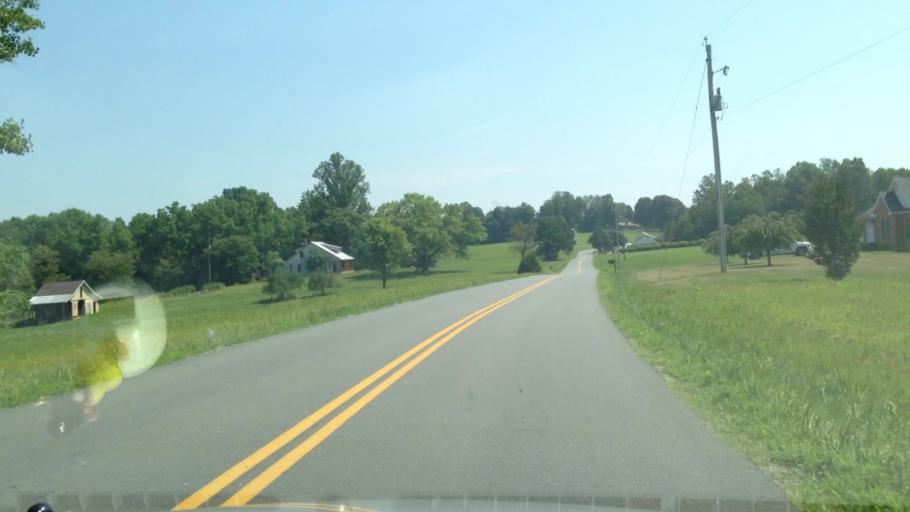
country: US
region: Virginia
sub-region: Patrick County
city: Patrick Springs
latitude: 36.5852
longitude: -80.1891
